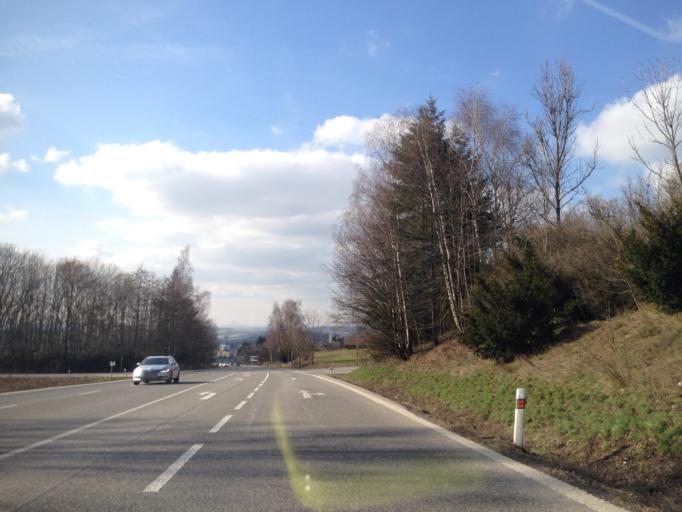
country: CZ
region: Kralovehradecky
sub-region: Okres Jicin
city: Sobotka
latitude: 50.4631
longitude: 15.2000
